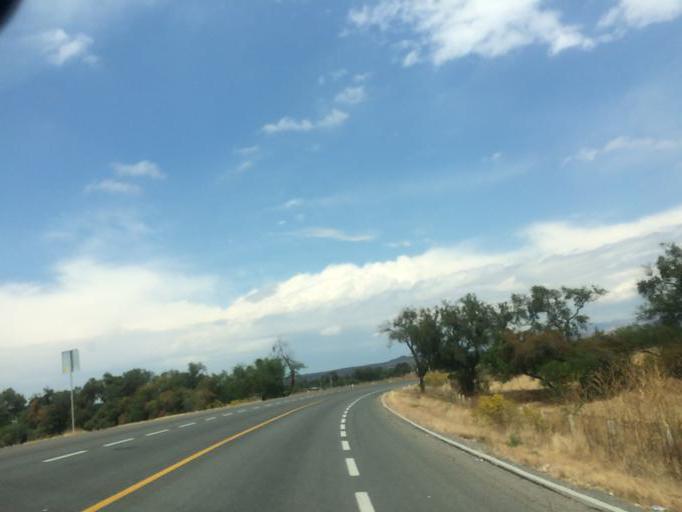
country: MX
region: Guanajuato
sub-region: Silao de la Victoria
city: Loma de Yerbabuena
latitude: 21.0282
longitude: -101.4579
